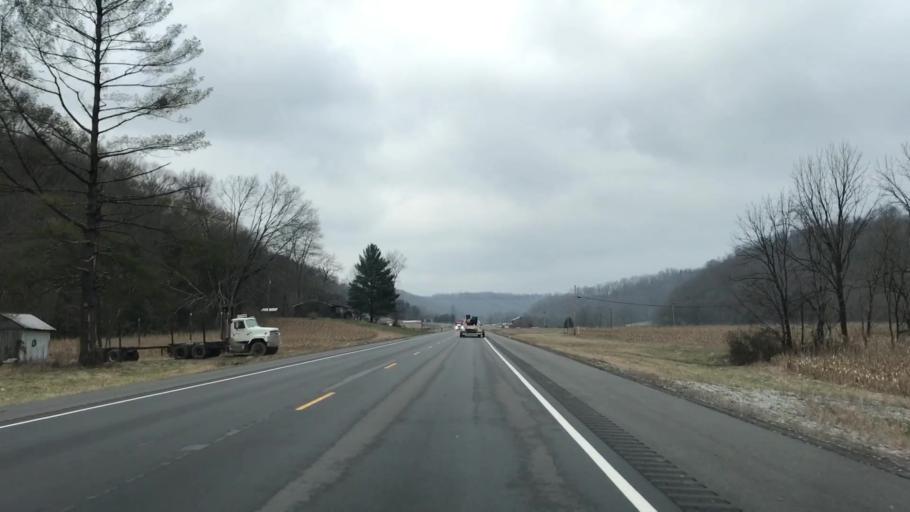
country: US
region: Kentucky
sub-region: Cumberland County
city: Burkesville
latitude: 36.8752
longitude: -85.3955
